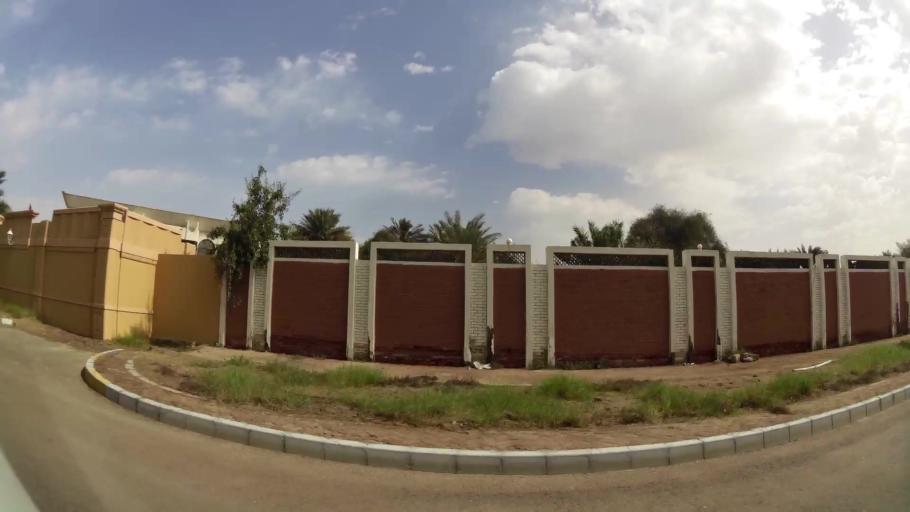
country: AE
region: Abu Dhabi
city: Abu Dhabi
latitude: 24.4397
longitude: 54.3626
